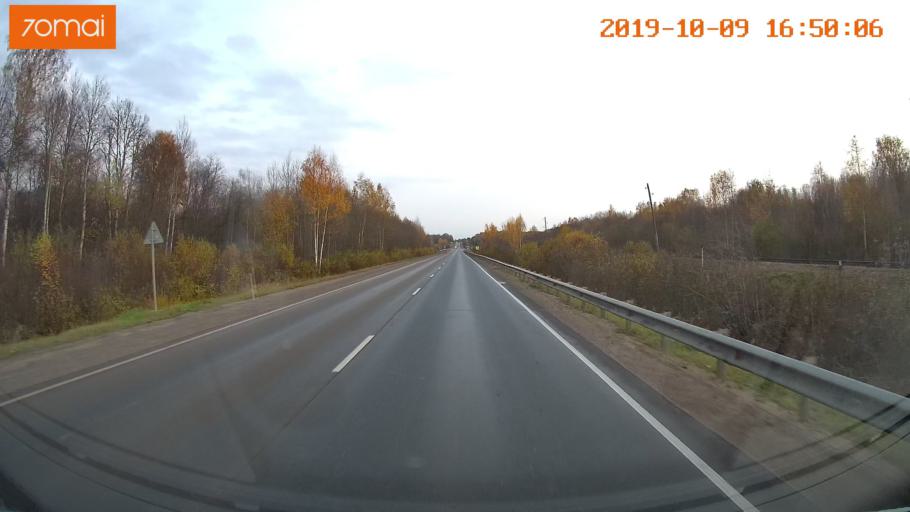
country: RU
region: Kostroma
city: Volgorechensk
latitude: 57.4057
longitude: 41.2044
